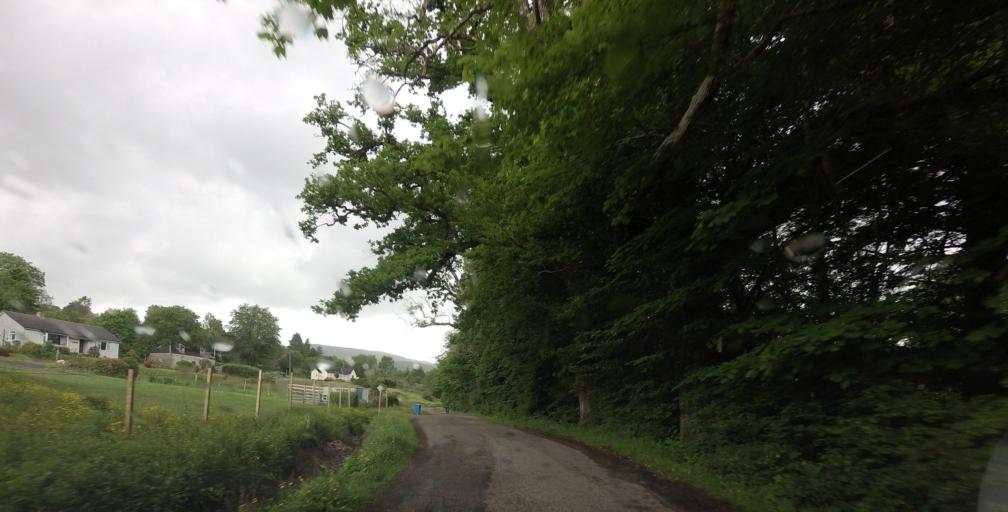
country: GB
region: Scotland
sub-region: Argyll and Bute
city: Oban
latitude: 56.6992
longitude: -5.5708
